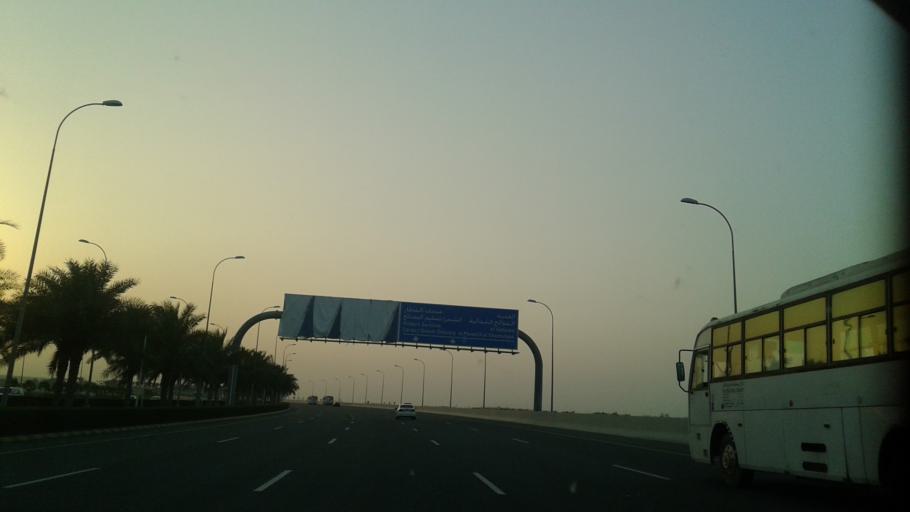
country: OM
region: Muhafazat Masqat
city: Bawshar
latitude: 23.6026
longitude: 58.3232
